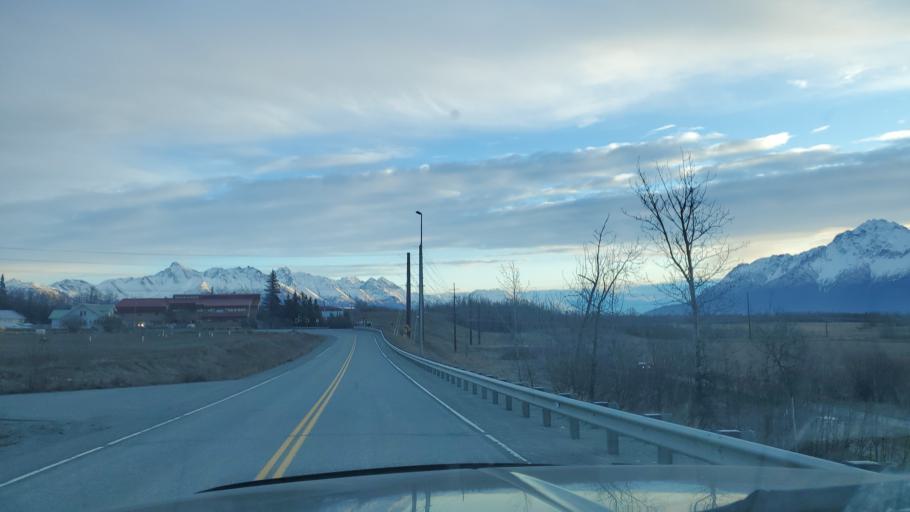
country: US
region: Alaska
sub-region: Matanuska-Susitna Borough
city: Gateway
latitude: 61.5655
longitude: -149.2571
